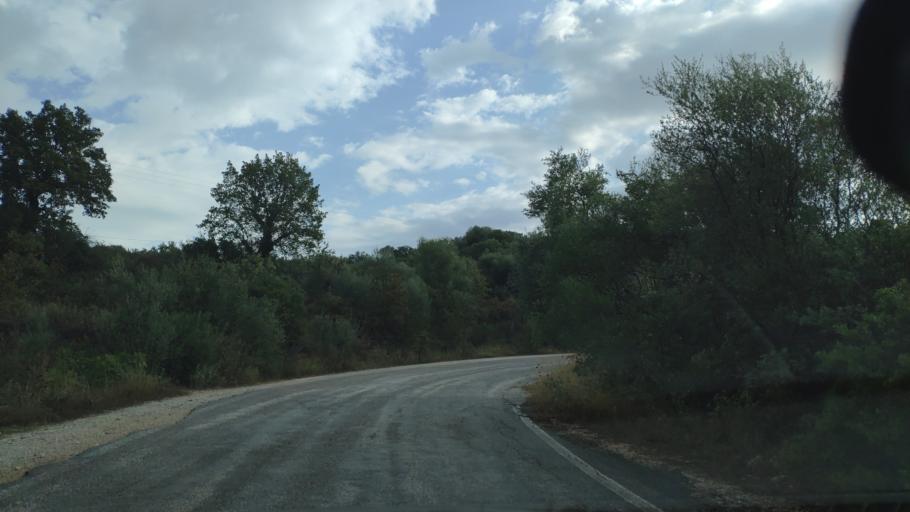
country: GR
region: West Greece
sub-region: Nomos Aitolias kai Akarnanias
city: Sardinia
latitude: 38.8879
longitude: 21.2150
